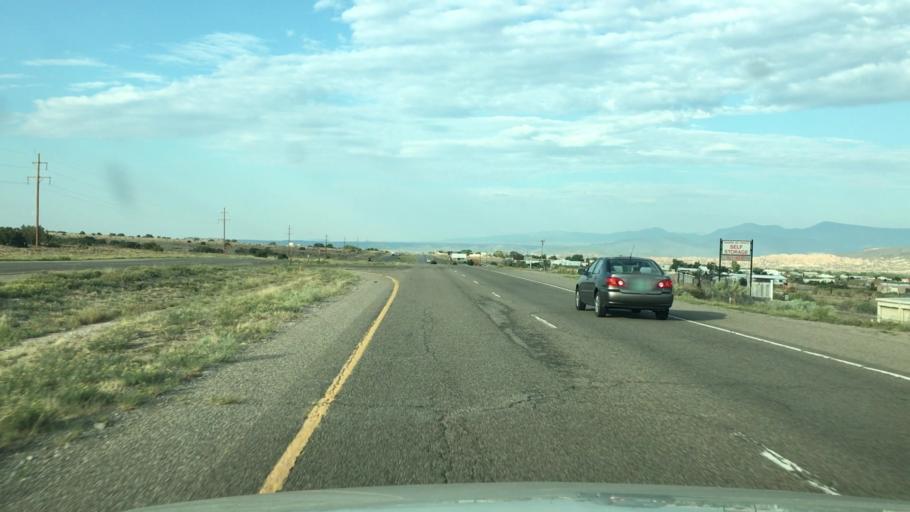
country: US
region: New Mexico
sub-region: Rio Arriba County
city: Ohkay Owingeh
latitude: 36.1236
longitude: -106.0108
